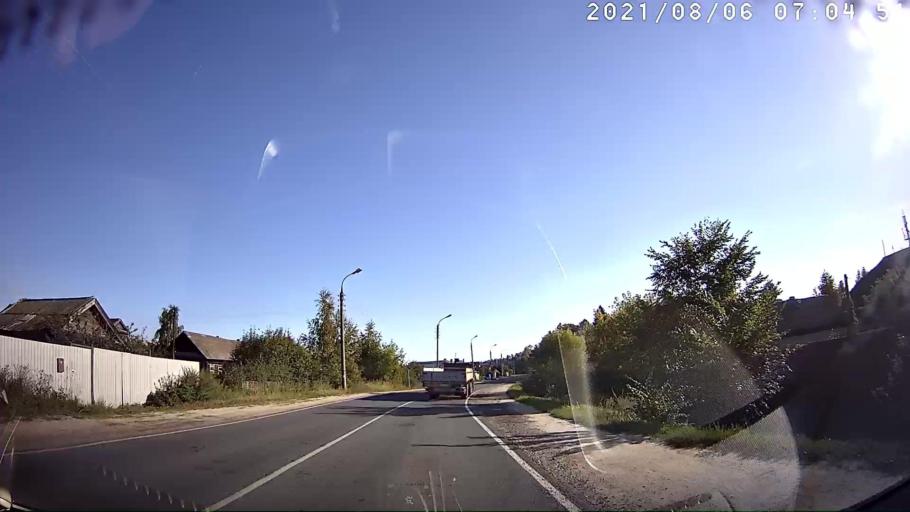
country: RU
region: Mariy-El
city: Yoshkar-Ola
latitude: 56.5499
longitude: 47.9838
